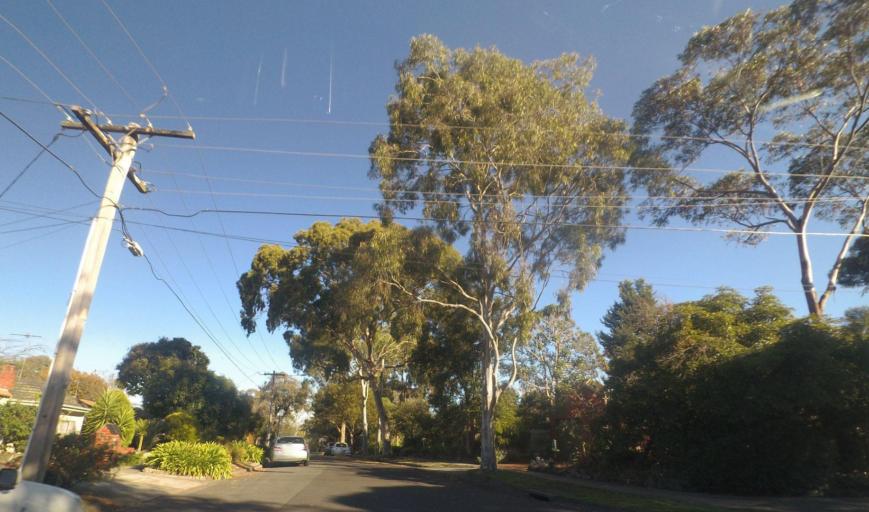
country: AU
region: Victoria
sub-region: Whitehorse
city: Blackburn North
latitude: -37.8124
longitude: 145.1473
